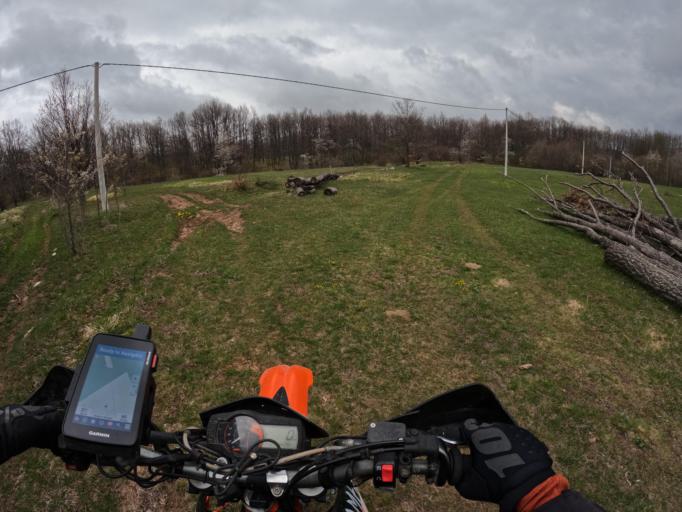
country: HR
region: Zadarska
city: Gracac
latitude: 44.3762
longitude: 15.9657
